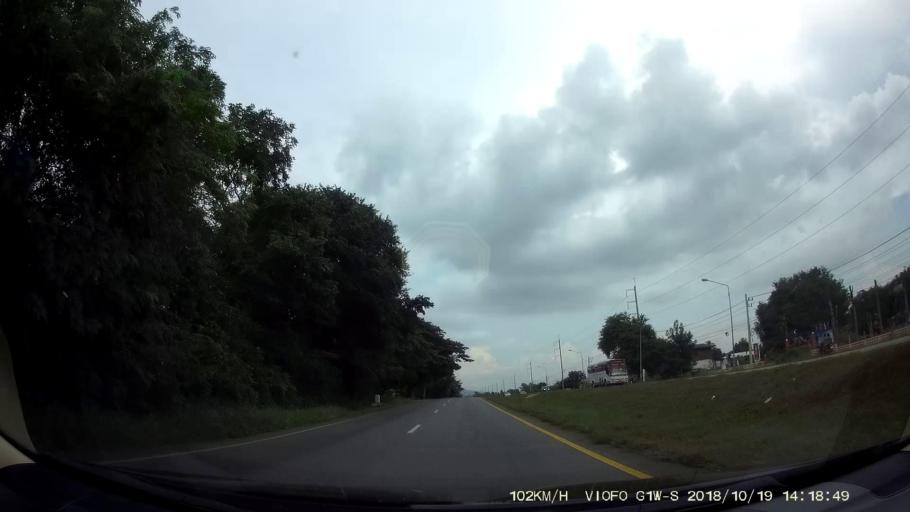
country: TH
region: Chaiyaphum
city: Kaeng Khro
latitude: 16.0202
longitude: 102.2390
